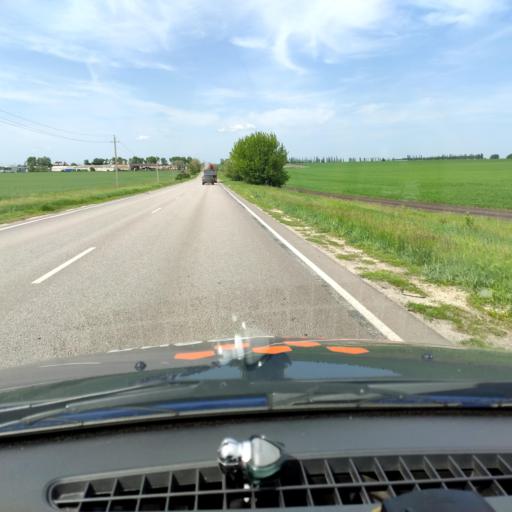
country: RU
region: Voronezj
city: Novaya Usman'
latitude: 51.5737
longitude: 39.3753
